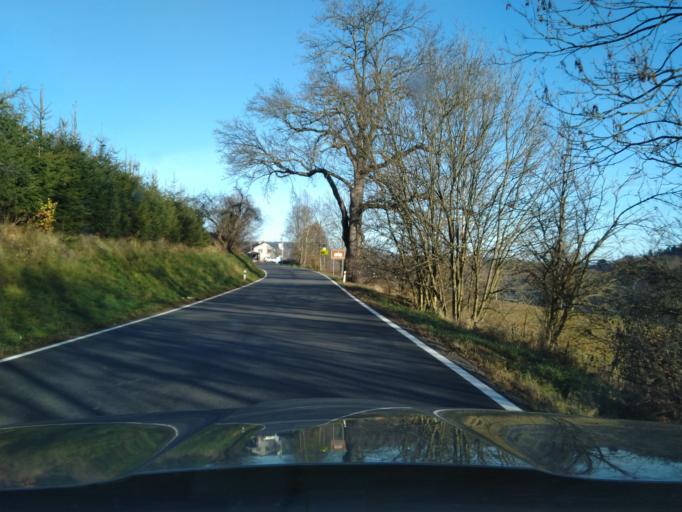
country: CZ
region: Jihocesky
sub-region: Okres Prachatice
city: Zdikov
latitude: 49.0951
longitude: 13.6913
